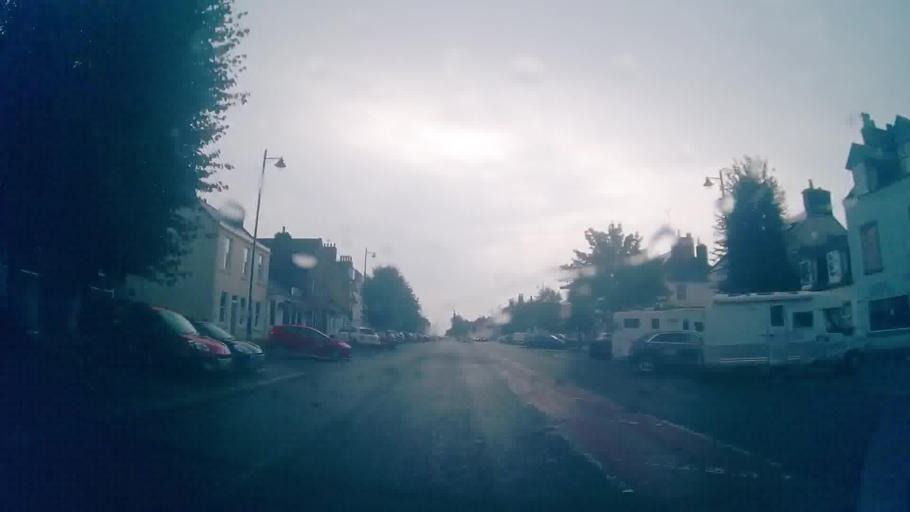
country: GB
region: Scotland
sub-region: Dumfries and Galloway
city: Thornhill
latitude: 55.2419
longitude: -3.7662
